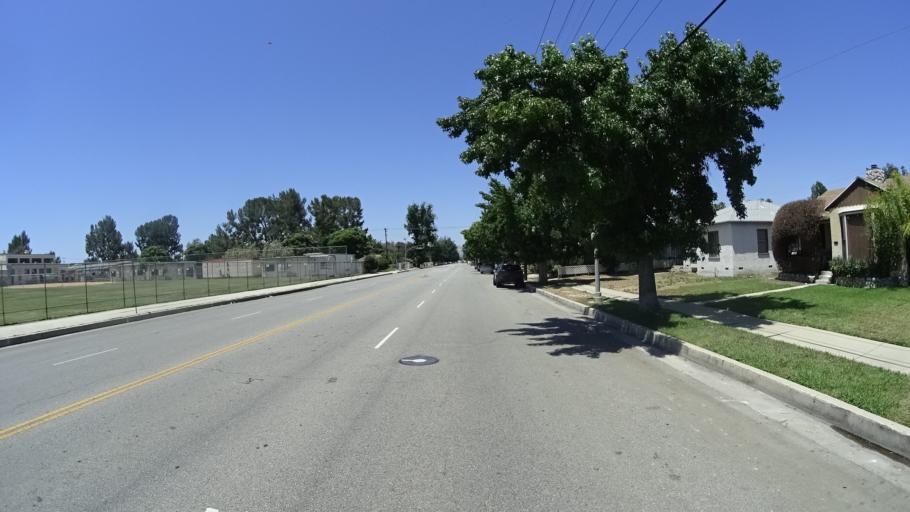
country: US
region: California
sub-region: Los Angeles County
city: Northridge
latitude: 34.1891
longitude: -118.5272
